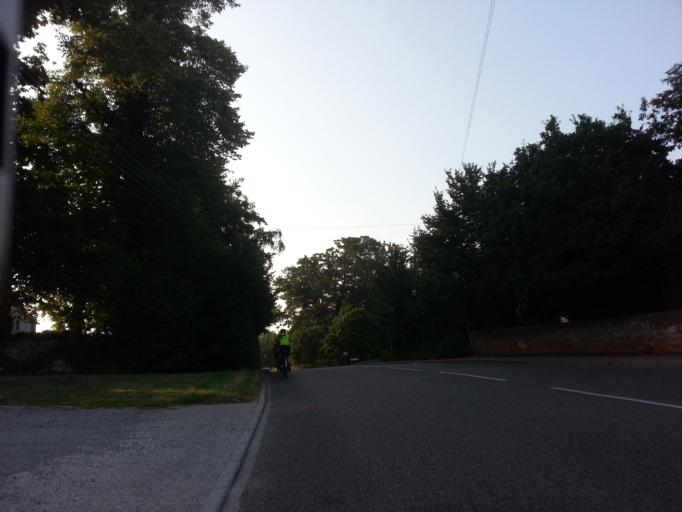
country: GB
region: England
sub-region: Suffolk
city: Bramford
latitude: 52.0785
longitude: 1.0951
